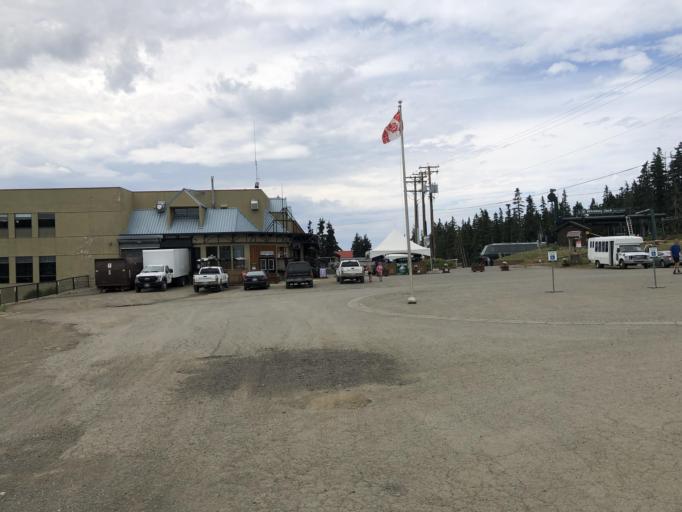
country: CA
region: British Columbia
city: Campbell River
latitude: 49.7412
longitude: -125.3023
